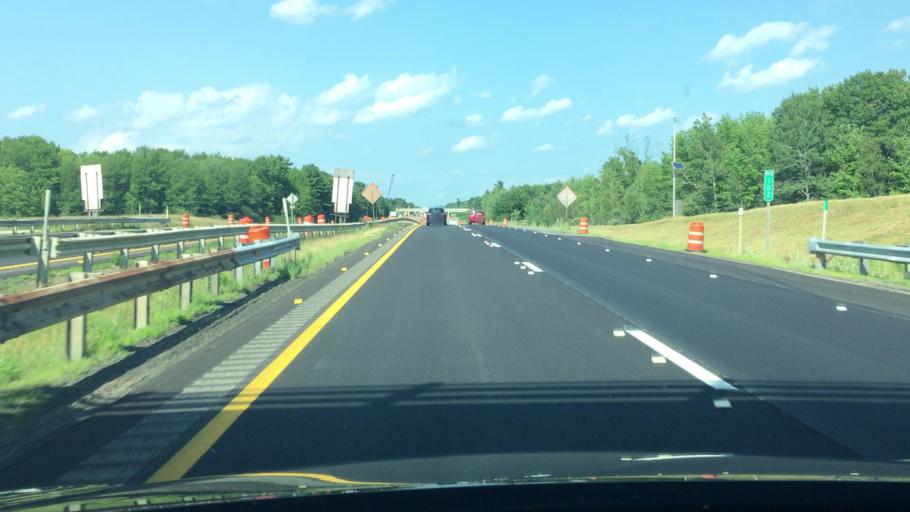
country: US
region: Maine
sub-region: Kennebec County
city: Gardiner
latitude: 44.2116
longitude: -69.8297
